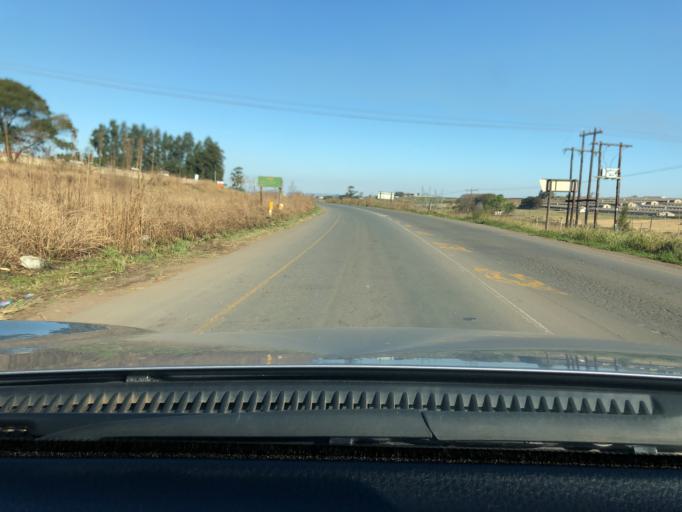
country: ZA
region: KwaZulu-Natal
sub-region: uMgungundlovu District Municipality
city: Camperdown
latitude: -29.7261
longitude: 30.4999
